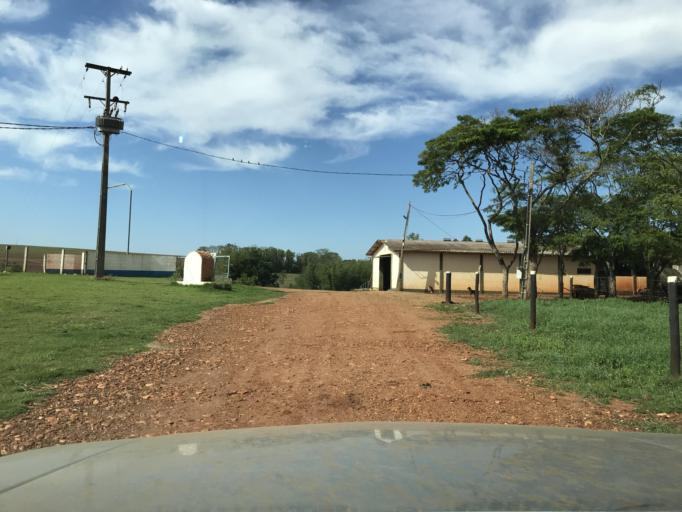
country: BR
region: Parana
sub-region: Palotina
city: Palotina
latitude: -24.1797
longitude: -53.8388
